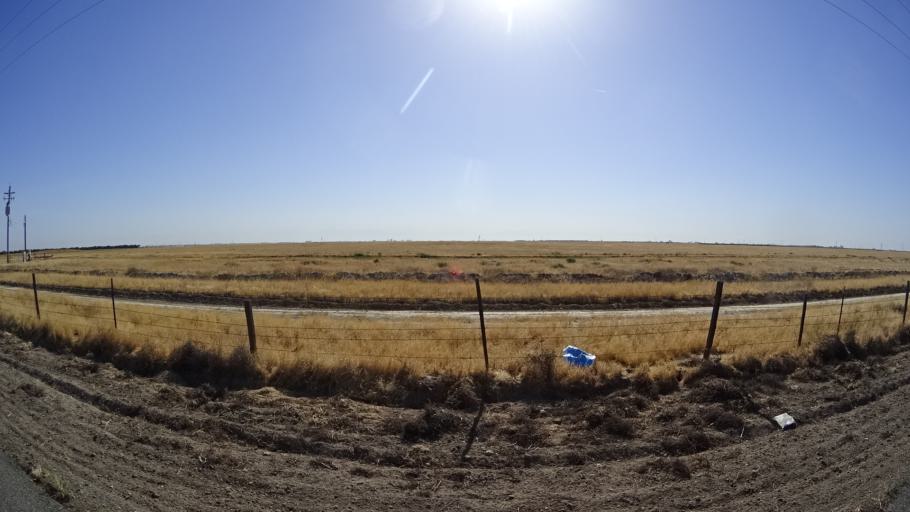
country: US
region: California
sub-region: Kings County
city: Corcoran
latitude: 36.1710
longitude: -119.5649
